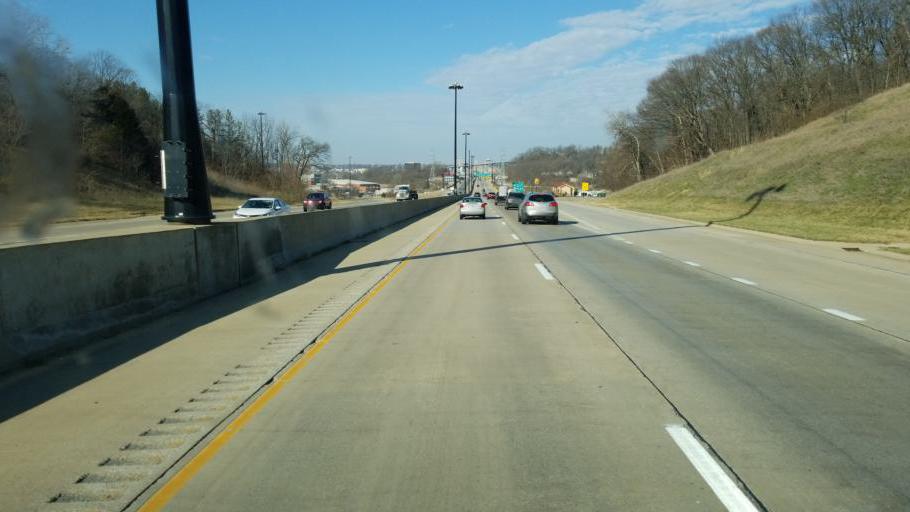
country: US
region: Illinois
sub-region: Tazewell County
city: East Peoria
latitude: 40.6593
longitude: -89.5655
